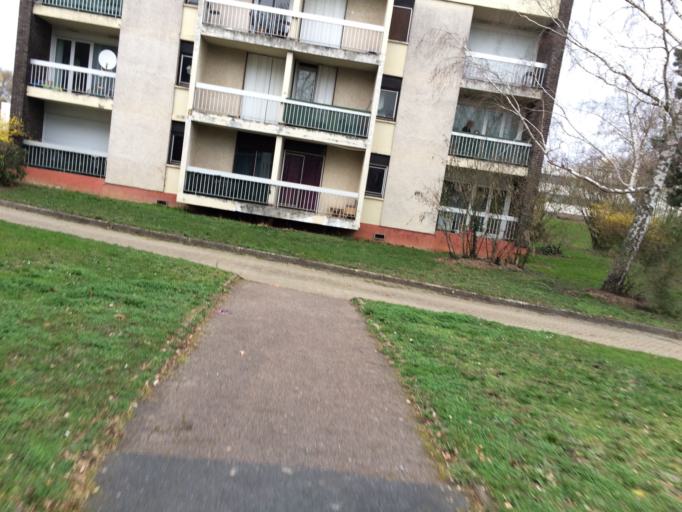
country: FR
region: Ile-de-France
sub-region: Departement de l'Essonne
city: Villebon-sur-Yvette
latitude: 48.7092
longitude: 2.2179
